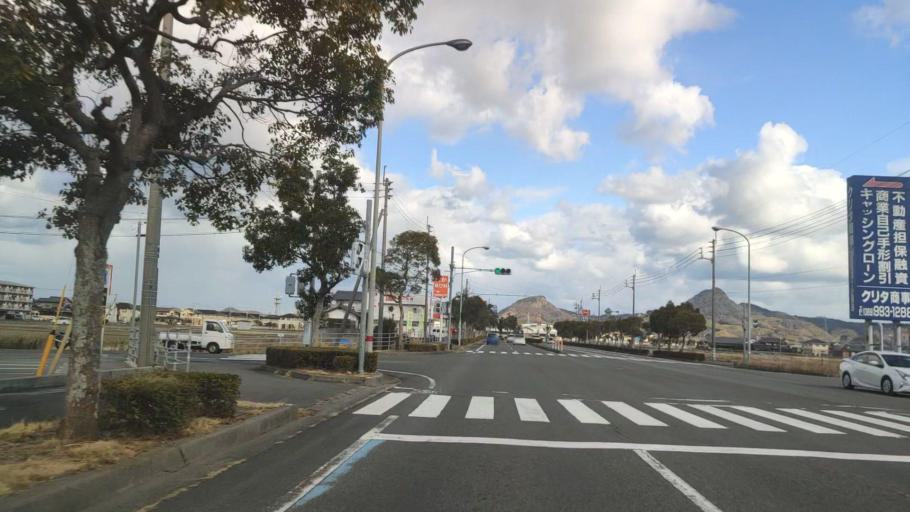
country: JP
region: Ehime
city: Hojo
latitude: 33.9643
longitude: 132.7785
